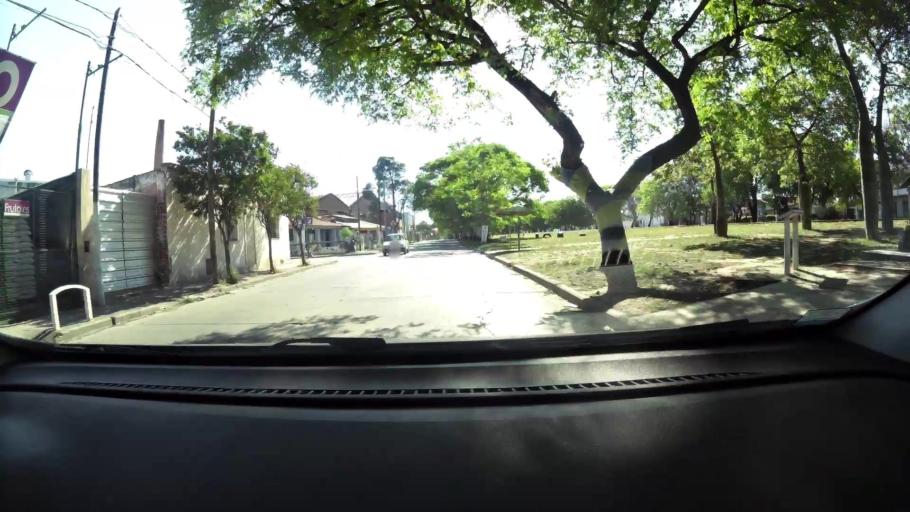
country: AR
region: Cordoba
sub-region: Departamento de Capital
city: Cordoba
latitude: -31.3908
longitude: -64.1404
